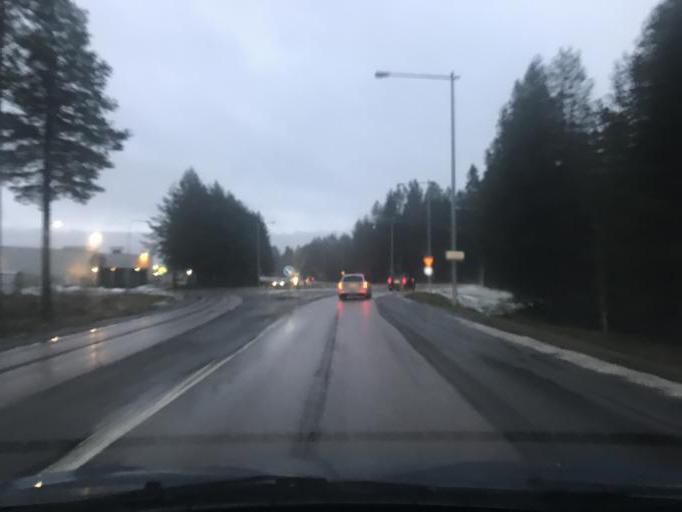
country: SE
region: Norrbotten
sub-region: Lulea Kommun
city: Gammelstad
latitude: 65.6197
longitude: 22.0364
